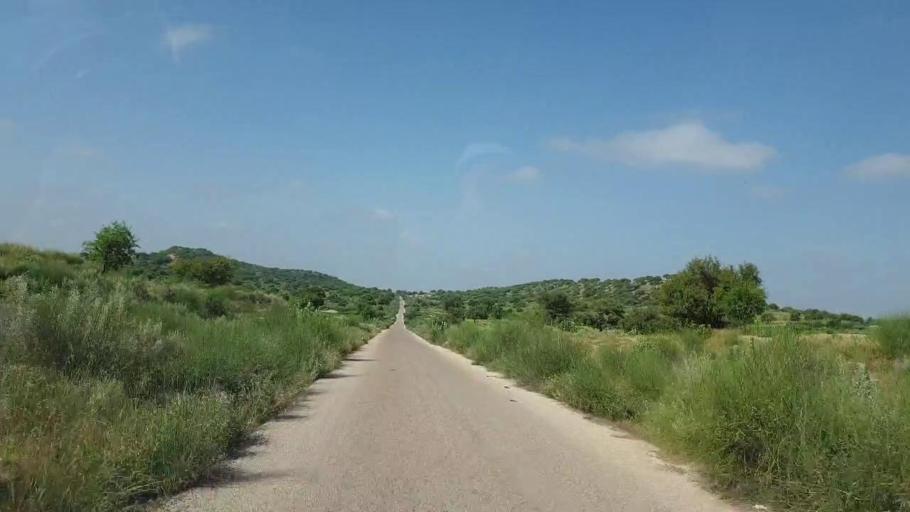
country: PK
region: Sindh
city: Mithi
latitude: 24.5520
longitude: 69.8893
